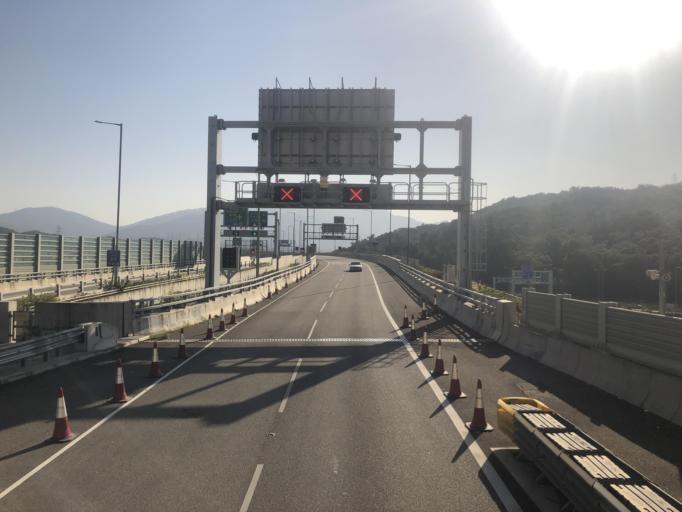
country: HK
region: Tai Po
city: Tai Po
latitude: 22.4841
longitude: 114.1549
